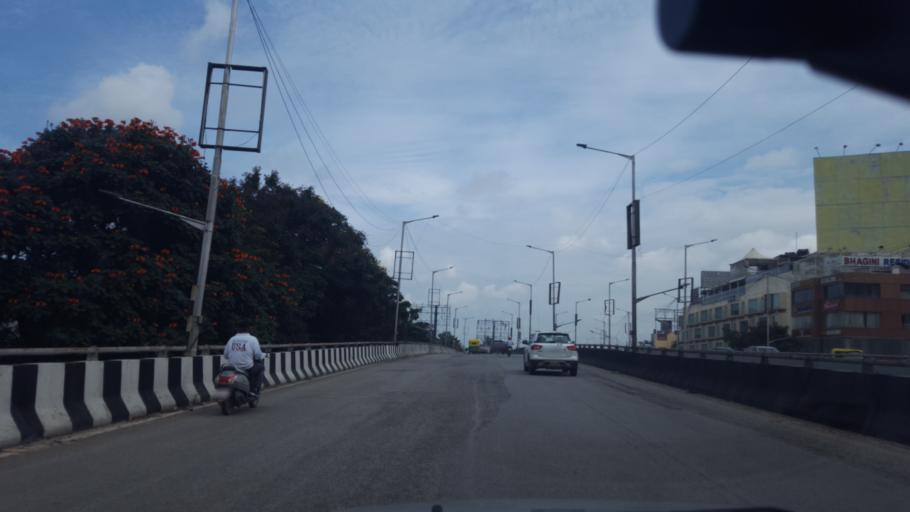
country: IN
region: Karnataka
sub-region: Bangalore Urban
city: Yelahanka
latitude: 13.0429
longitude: 77.6126
